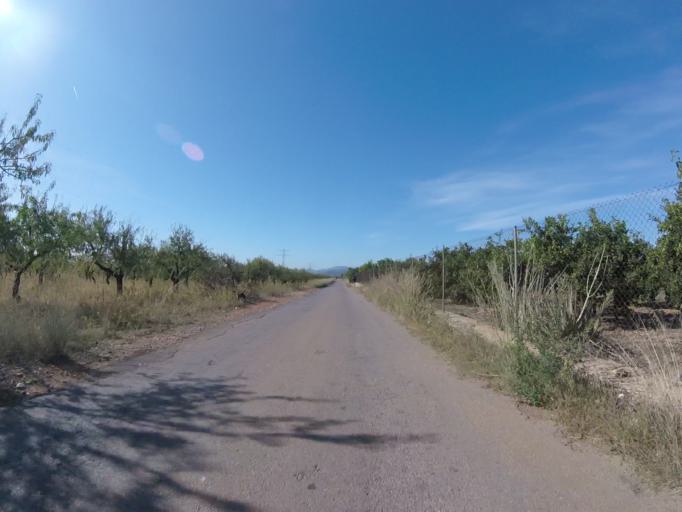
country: ES
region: Valencia
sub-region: Provincia de Castello
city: Torreblanca
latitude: 40.2125
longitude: 0.2128
